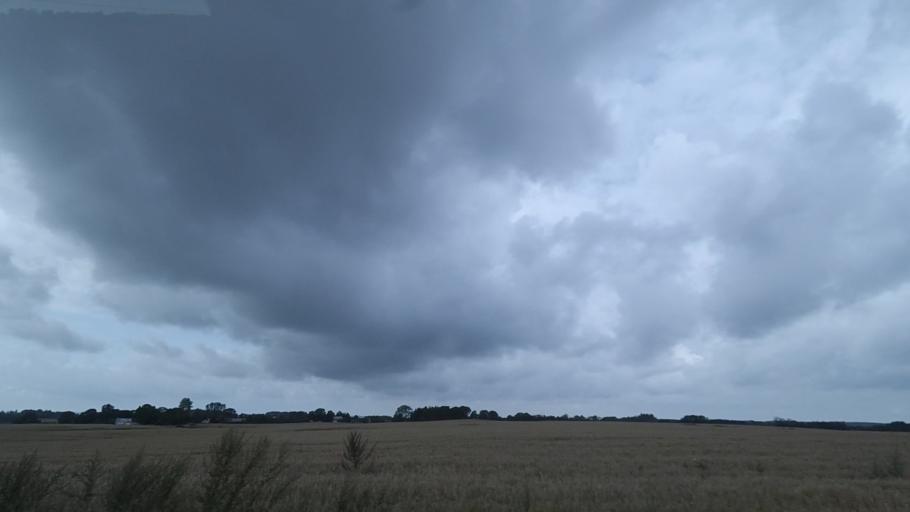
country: DK
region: Central Jutland
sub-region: Syddjurs Kommune
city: Ryomgard
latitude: 56.3924
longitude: 10.5640
